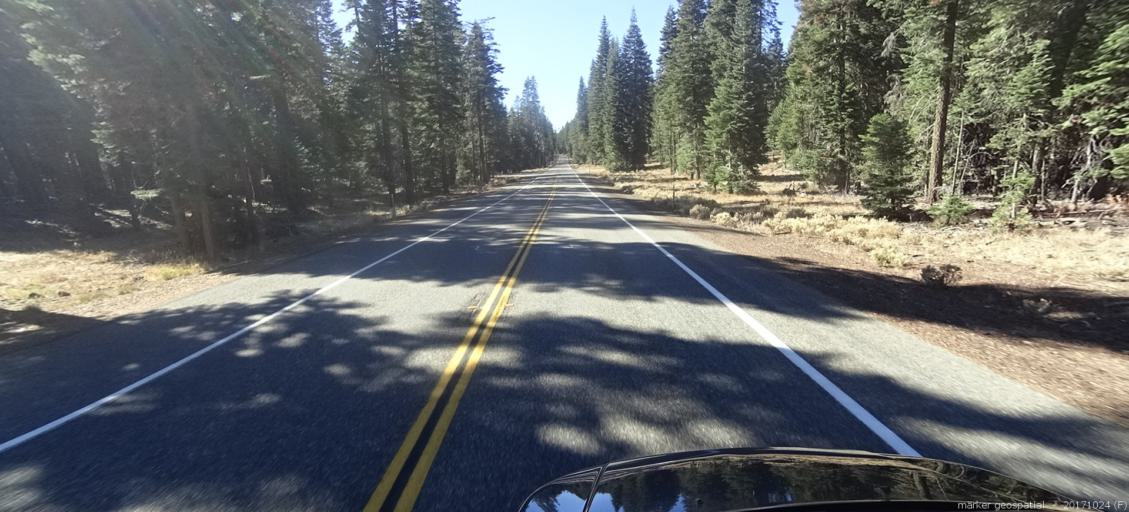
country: US
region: California
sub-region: Shasta County
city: Burney
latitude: 40.5910
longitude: -121.5400
